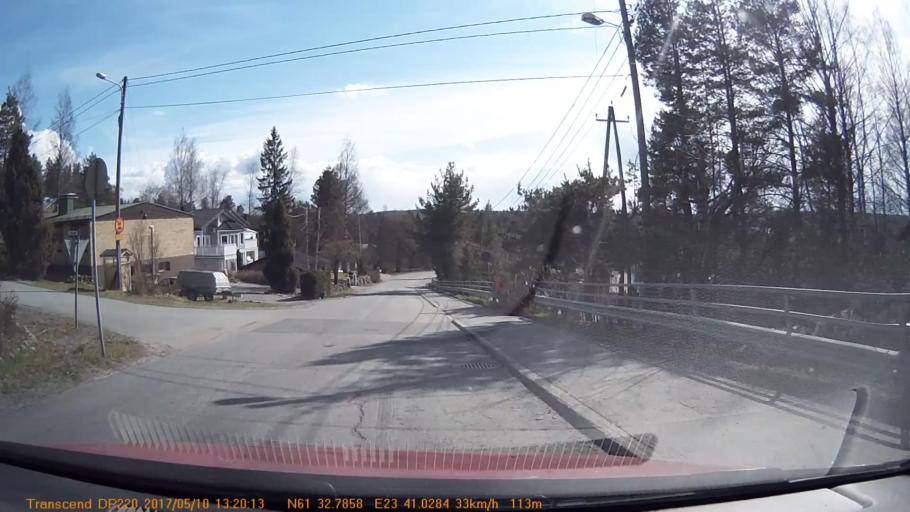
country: FI
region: Pirkanmaa
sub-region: Tampere
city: Yloejaervi
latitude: 61.5464
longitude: 23.6838
